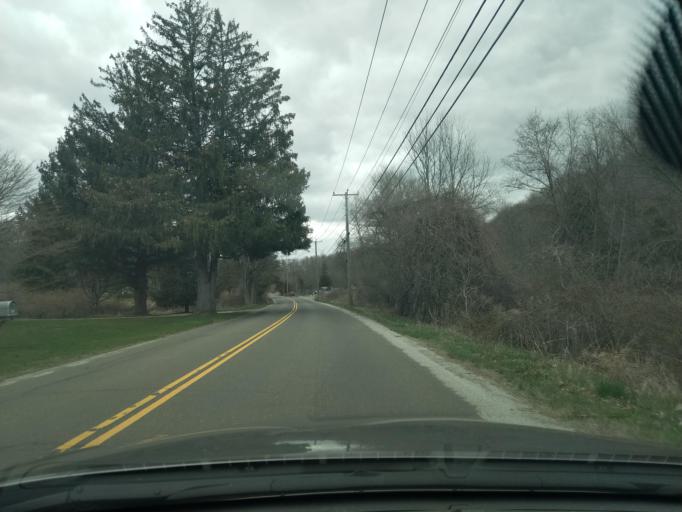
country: US
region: Connecticut
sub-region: Fairfield County
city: Newtown
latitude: 41.3435
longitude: -73.2933
